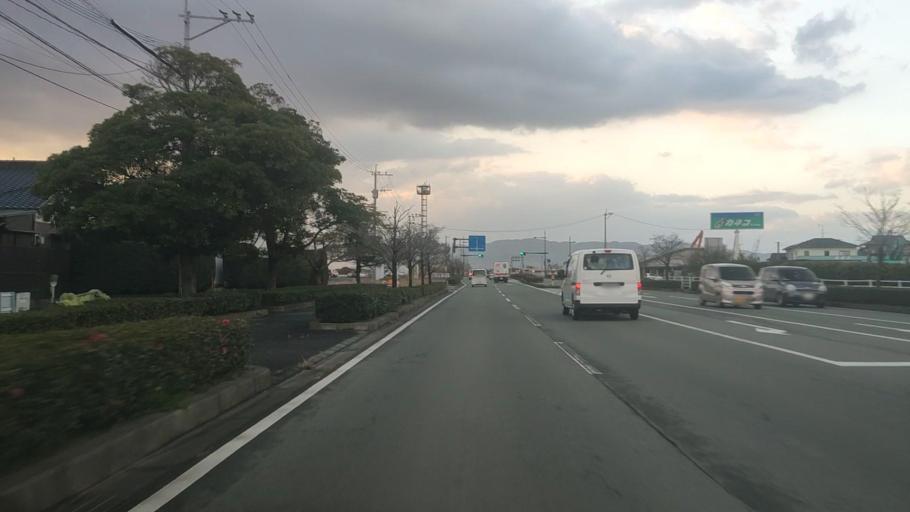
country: JP
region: Kumamoto
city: Kumamoto
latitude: 32.7591
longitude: 130.7059
